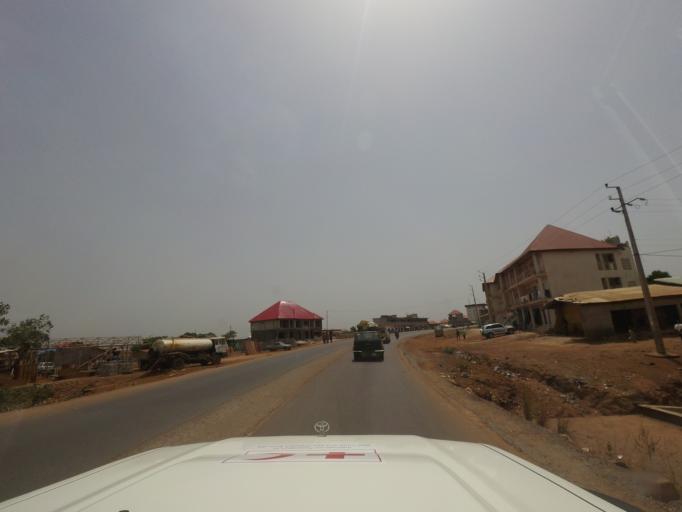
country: GN
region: Kindia
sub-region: Coyah
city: Coyah
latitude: 9.7243
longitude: -13.4421
